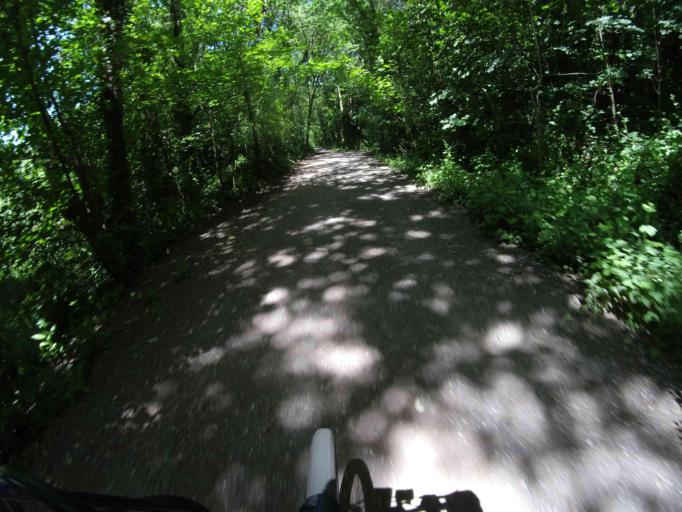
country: GB
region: England
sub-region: Devon
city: Bovey Tracey
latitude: 50.6040
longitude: -3.6979
